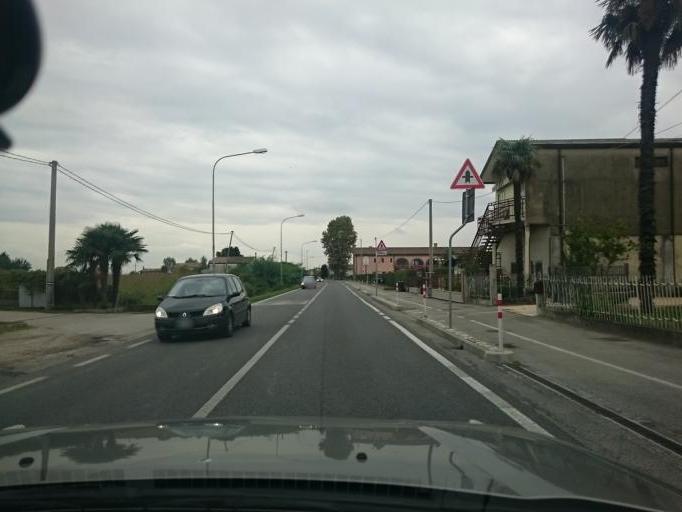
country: IT
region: Veneto
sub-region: Provincia di Padova
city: Arzergrande
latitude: 45.2709
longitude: 12.0280
